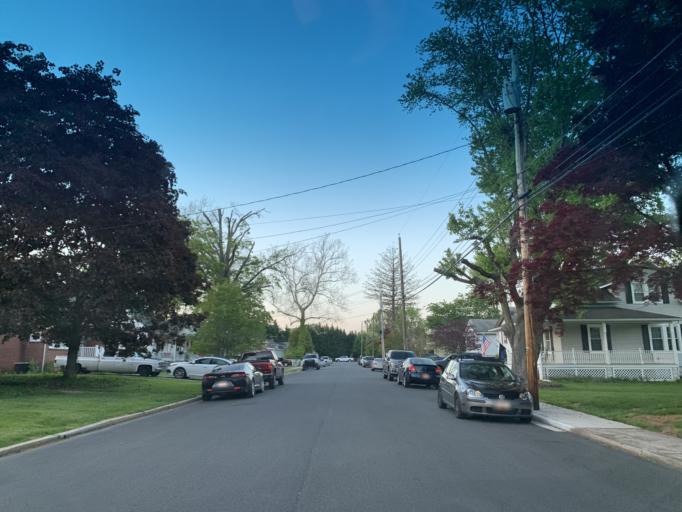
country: US
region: Maryland
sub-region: Harford County
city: Aberdeen
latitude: 39.5090
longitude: -76.1713
